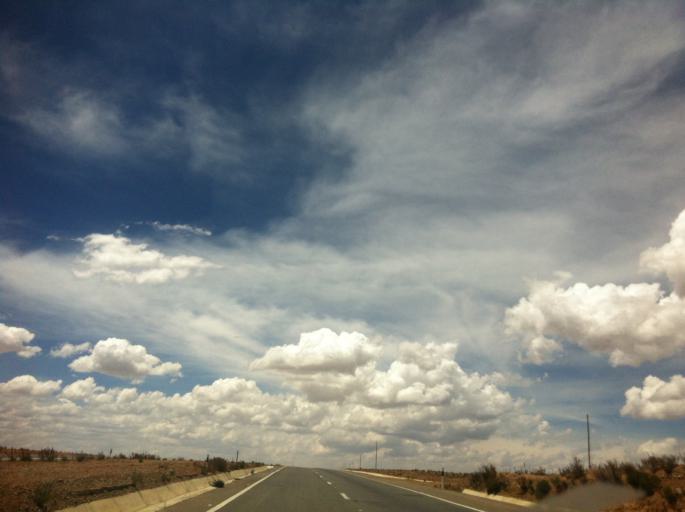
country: BO
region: La Paz
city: Patacamaya
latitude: -17.0863
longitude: -68.0132
